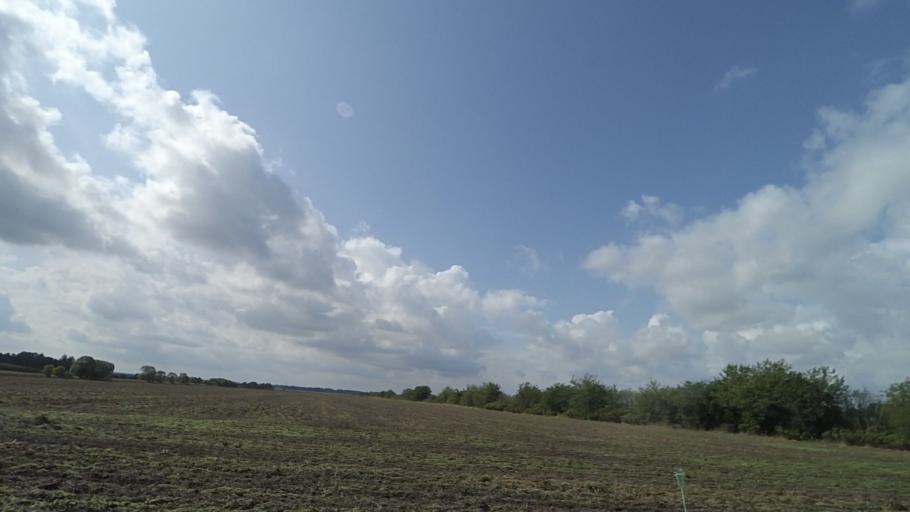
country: DK
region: Central Jutland
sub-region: Norddjurs Kommune
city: Allingabro
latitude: 56.5075
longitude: 10.3989
